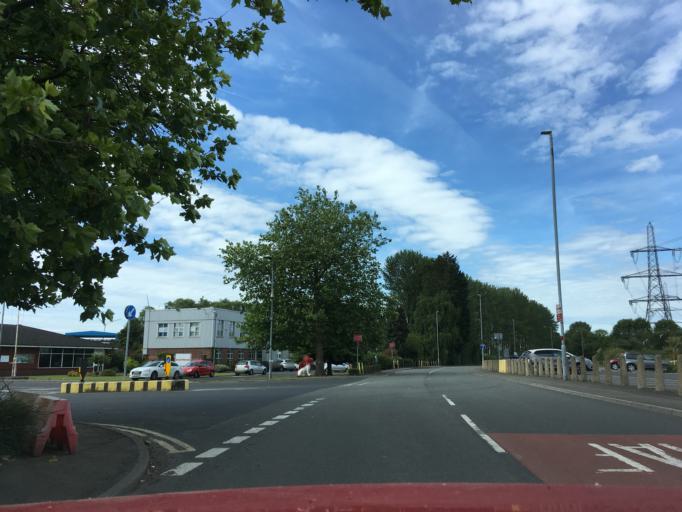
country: GB
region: Wales
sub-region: Newport
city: Nash
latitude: 51.5674
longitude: -2.9619
